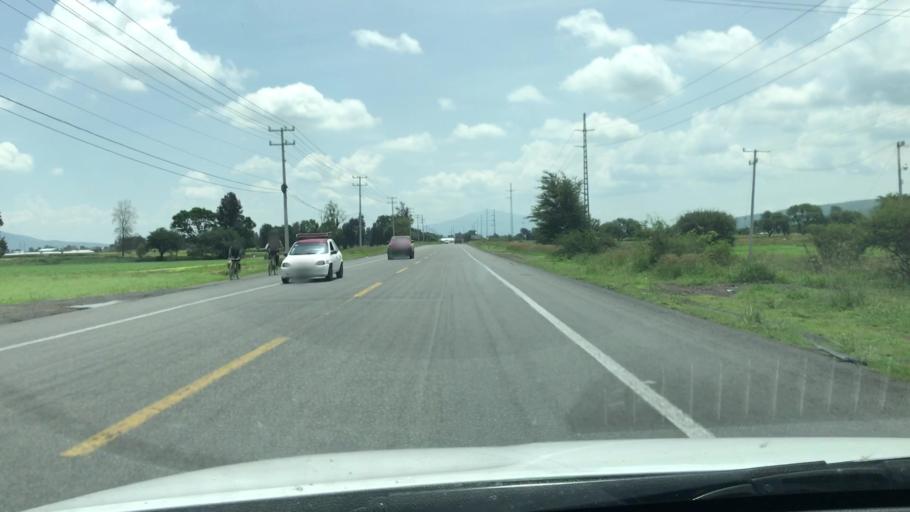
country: MX
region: Michoacan
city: Tanhuato de Guerrero
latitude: 20.2812
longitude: -102.3543
